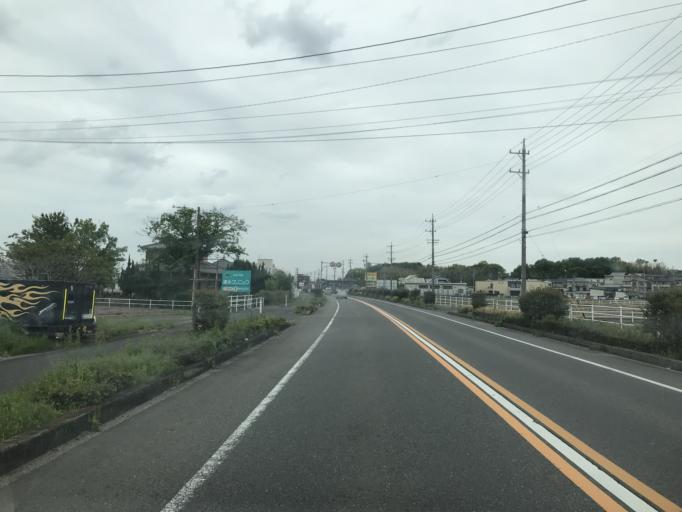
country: JP
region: Aichi
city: Kasugai
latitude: 35.2755
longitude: 136.9819
